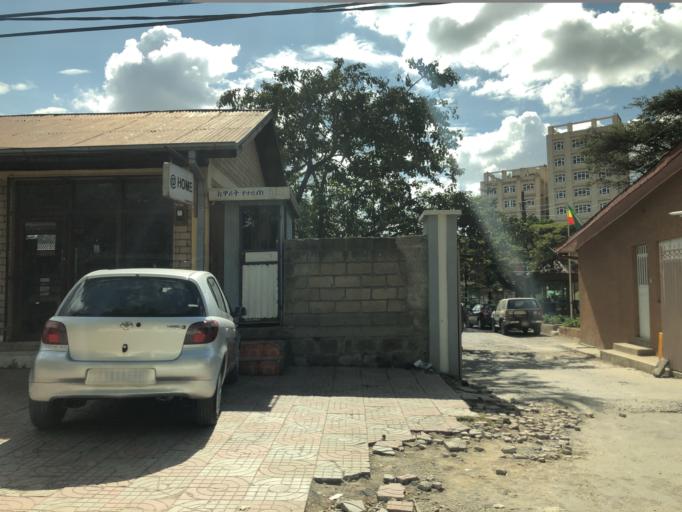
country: ET
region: Adis Abeba
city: Addis Ababa
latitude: 8.9955
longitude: 38.7795
